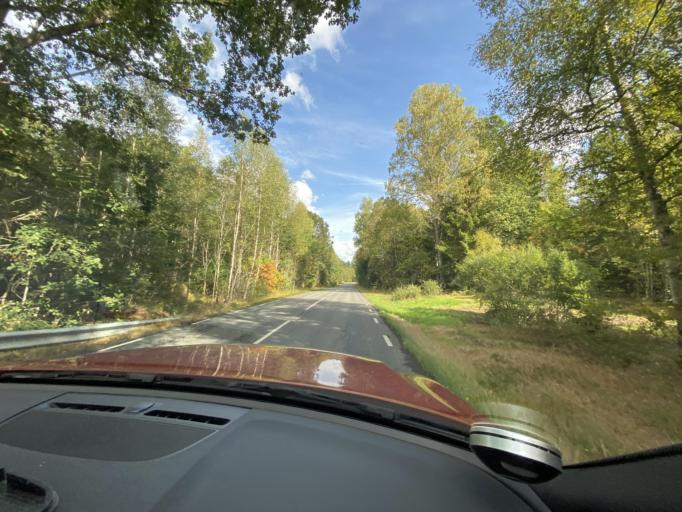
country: SE
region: Skane
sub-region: Hassleholms Kommun
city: Bjarnum
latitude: 56.3550
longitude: 13.7439
